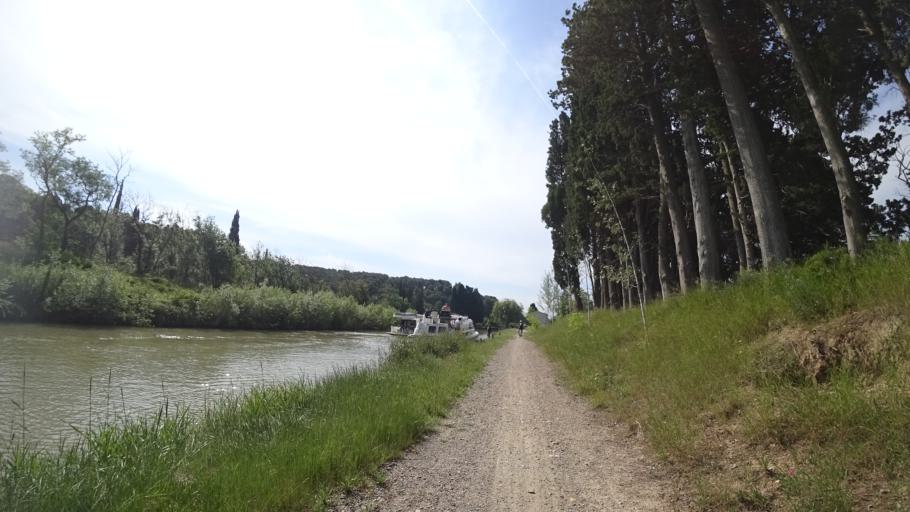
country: FR
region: Languedoc-Roussillon
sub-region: Departement de l'Herault
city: Olonzac
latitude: 43.2516
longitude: 2.7560
